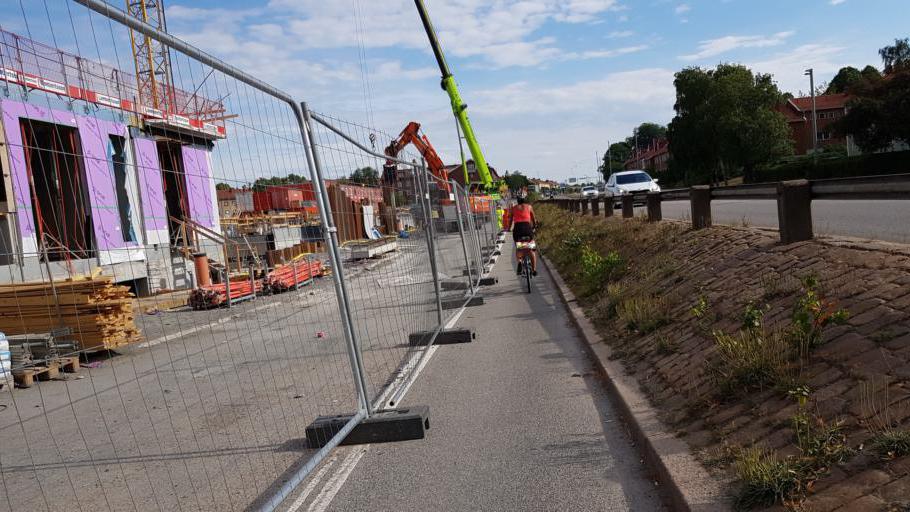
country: SE
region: Vaestra Goetaland
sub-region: Goteborg
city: Eriksbo
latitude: 57.7216
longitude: 12.0250
